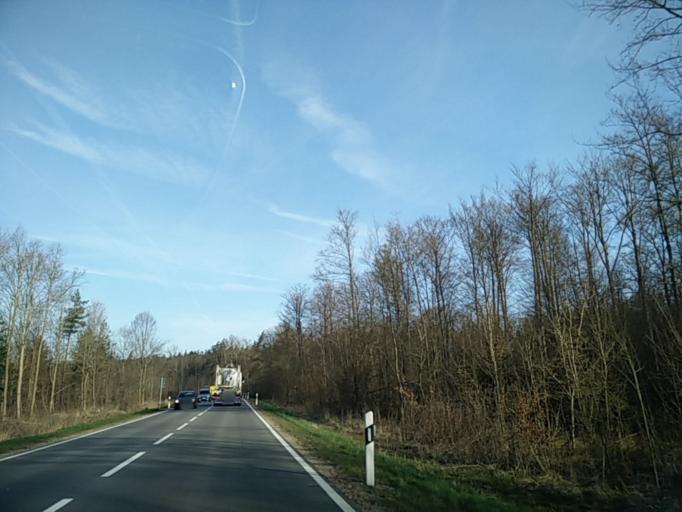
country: DE
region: Baden-Wuerttemberg
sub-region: Regierungsbezirk Stuttgart
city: Weil im Schonbuch
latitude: 48.6075
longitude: 9.0493
